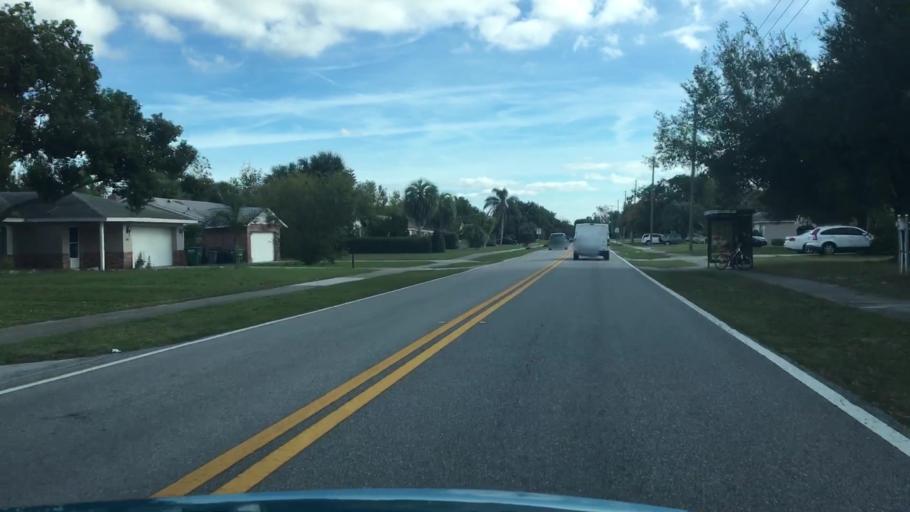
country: US
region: Florida
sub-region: Volusia County
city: Deltona
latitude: 28.8906
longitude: -81.2460
